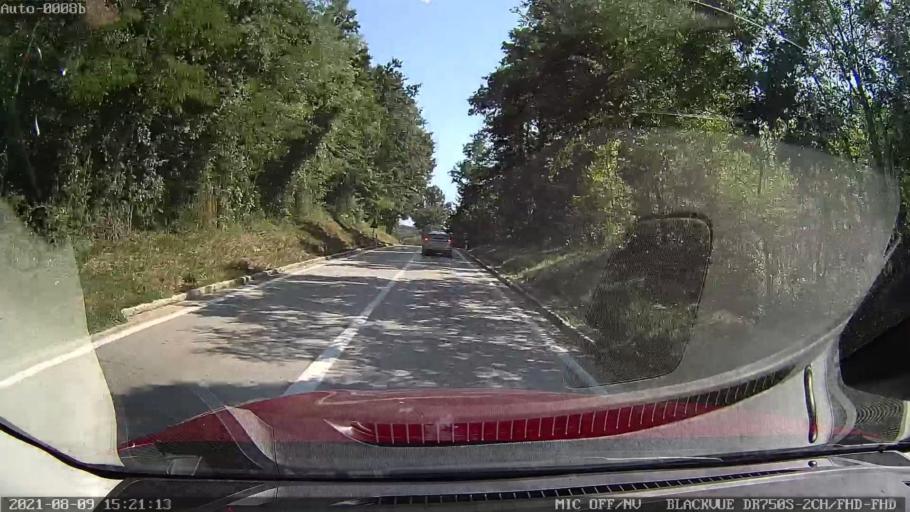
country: HR
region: Istarska
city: Pazin
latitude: 45.2008
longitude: 13.8954
